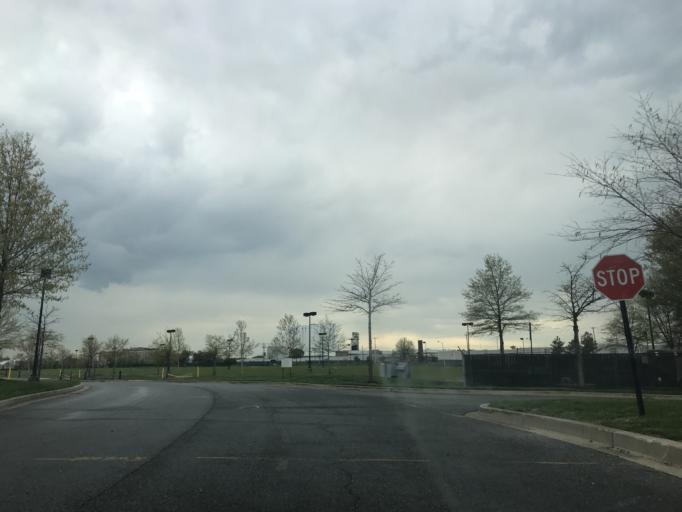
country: US
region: Maryland
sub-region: City of Baltimore
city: Baltimore
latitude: 39.2623
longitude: -76.6087
